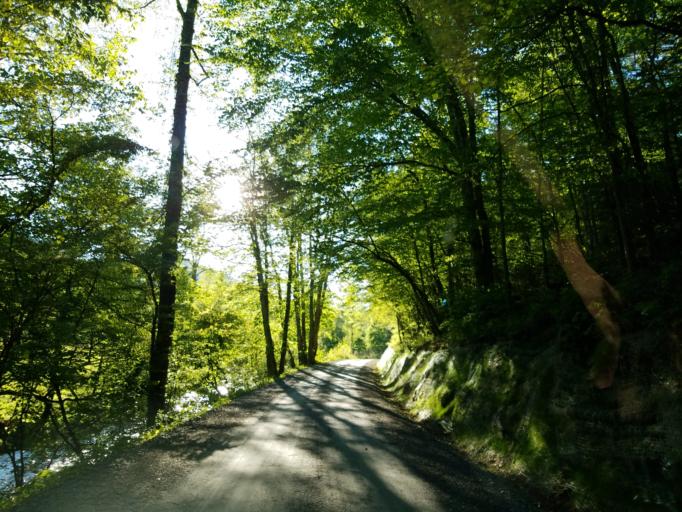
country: US
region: Georgia
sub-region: Fannin County
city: Blue Ridge
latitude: 34.7571
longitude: -84.2604
